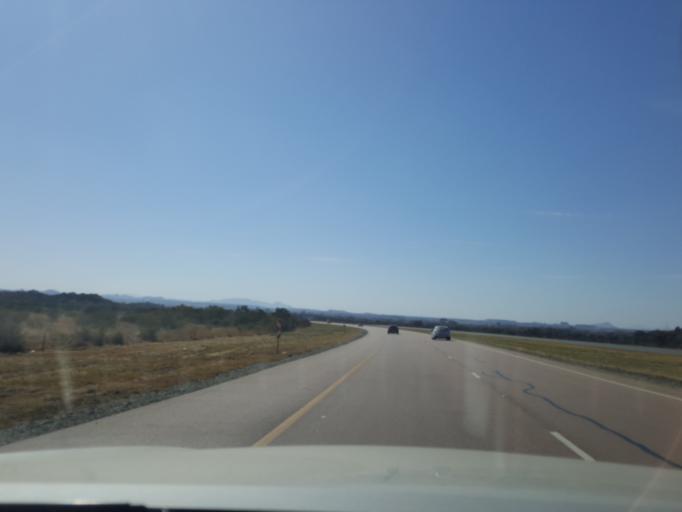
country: ZA
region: North-West
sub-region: Bojanala Platinum District Municipality
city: Brits
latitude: -25.7457
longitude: 27.5278
